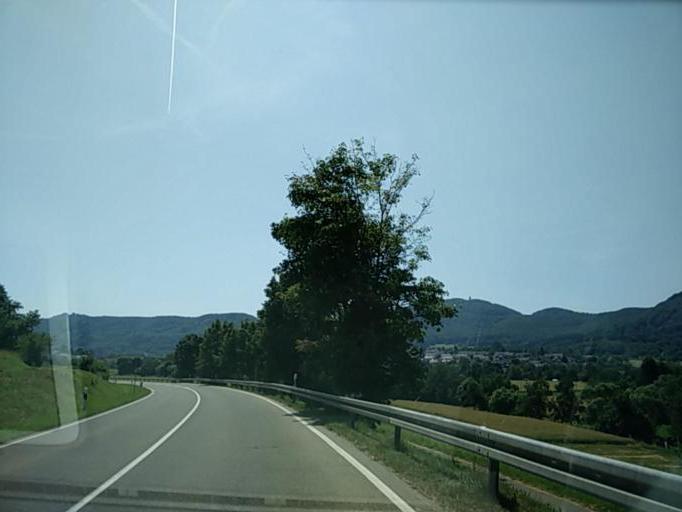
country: DE
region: Baden-Wuerttemberg
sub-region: Tuebingen Region
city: Gomaringen
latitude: 48.4417
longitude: 9.1407
